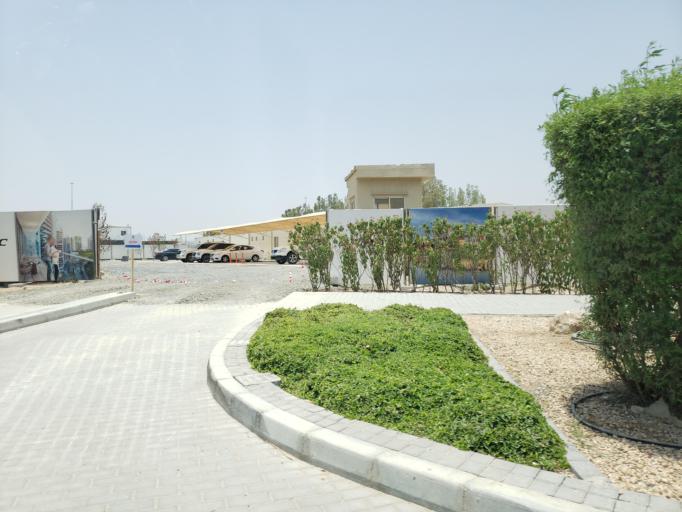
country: AE
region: Dubai
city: Dubai
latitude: 25.0283
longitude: 55.2515
